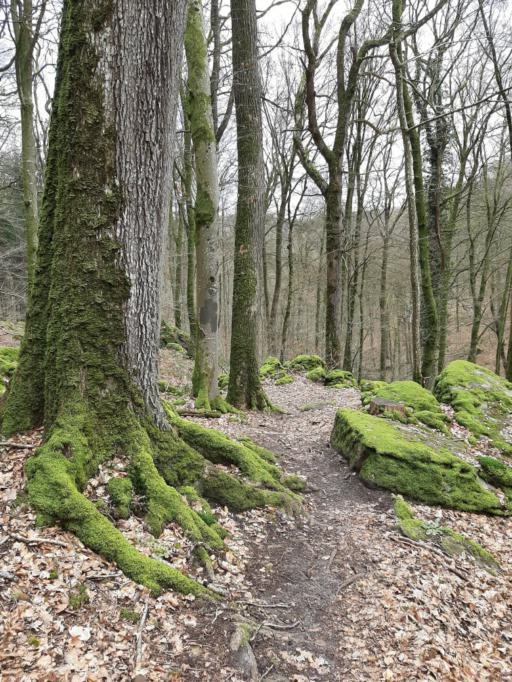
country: LU
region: Grevenmacher
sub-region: Canton d'Echternach
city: Beaufort
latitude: 49.8233
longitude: 6.3106
